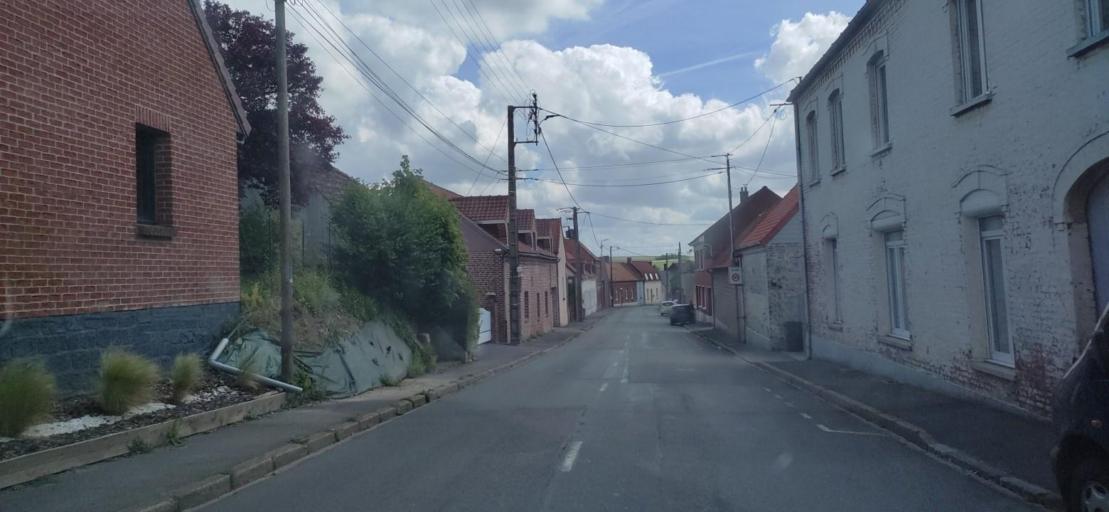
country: FR
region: Nord-Pas-de-Calais
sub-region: Departement du Pas-de-Calais
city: Therouanne
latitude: 50.6407
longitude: 2.2576
